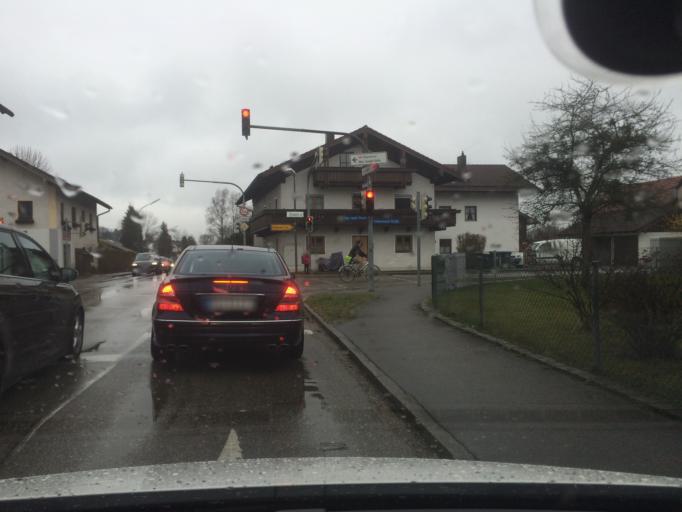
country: DE
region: Bavaria
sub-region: Upper Bavaria
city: Grosskarolinenfeld
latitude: 47.8858
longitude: 12.0739
